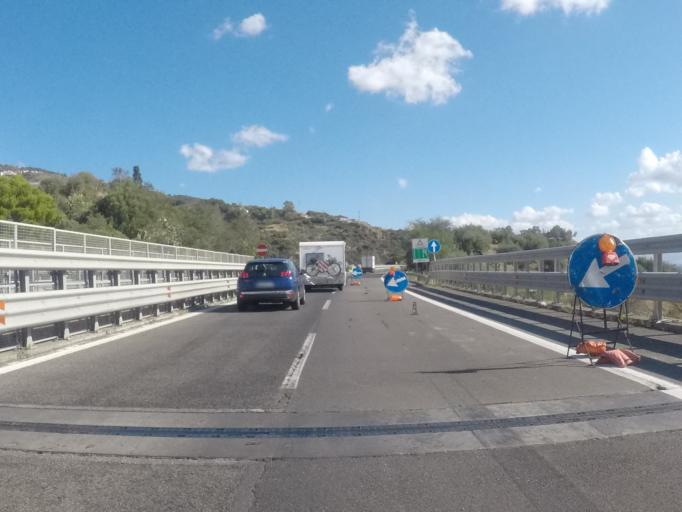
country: IT
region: Sicily
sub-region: Messina
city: Ali Terme
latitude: 38.0061
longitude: 15.4221
